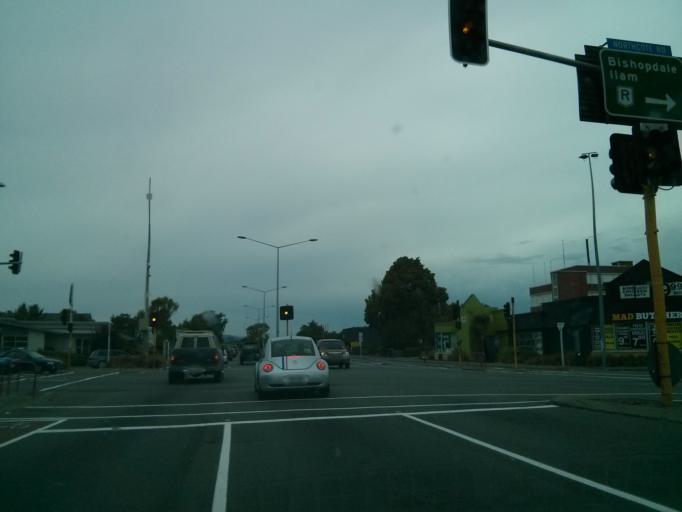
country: NZ
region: Canterbury
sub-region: Christchurch City
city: Christchurch
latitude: -43.4843
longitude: 172.6163
